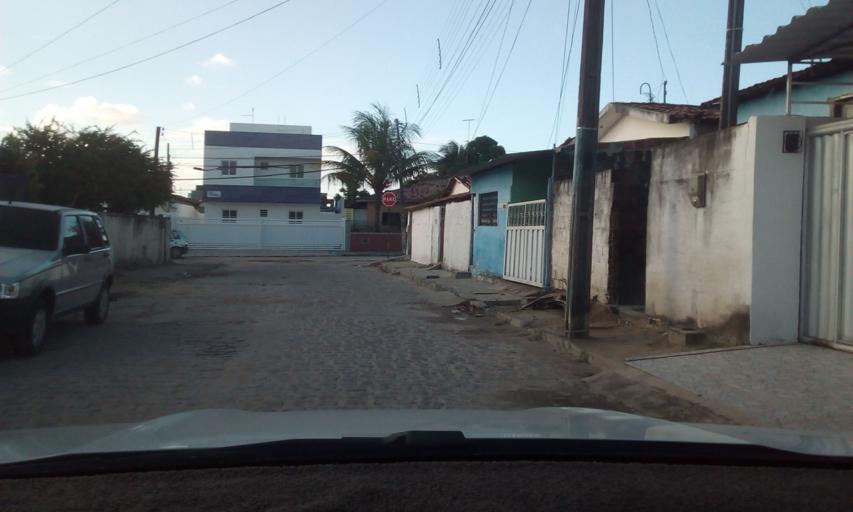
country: BR
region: Paraiba
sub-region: Joao Pessoa
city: Joao Pessoa
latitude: -7.1843
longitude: -34.8377
